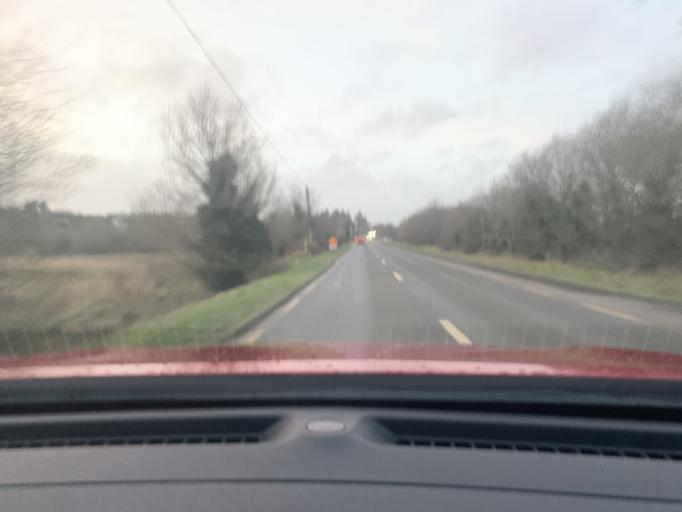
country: IE
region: Connaught
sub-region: Sligo
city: Ballymote
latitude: 54.0847
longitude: -8.3826
